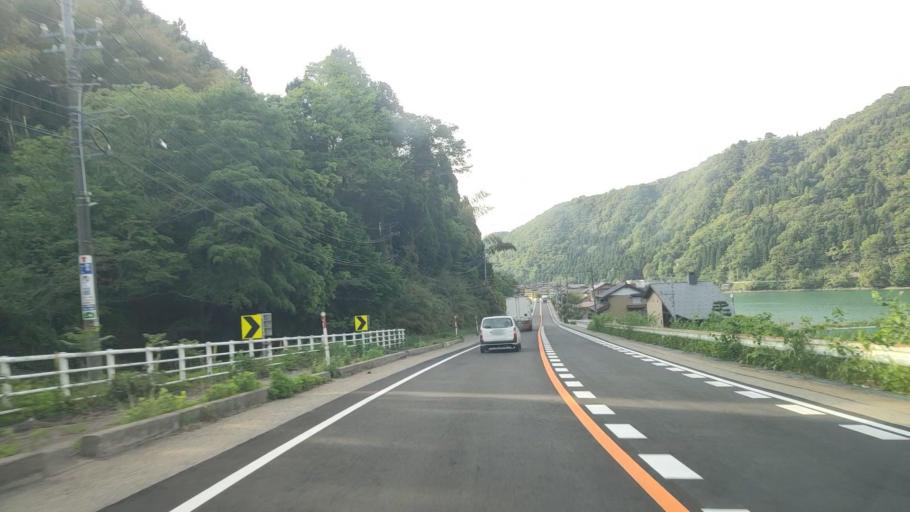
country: JP
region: Toyama
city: Yatsuomachi-higashikumisaka
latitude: 36.5479
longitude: 137.2254
